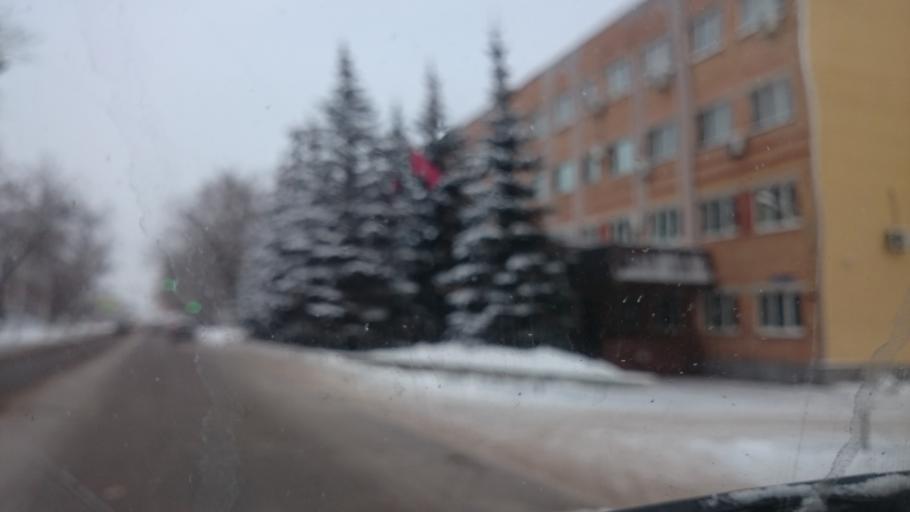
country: RU
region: Tula
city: Mendeleyevskiy
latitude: 54.1403
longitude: 37.5866
